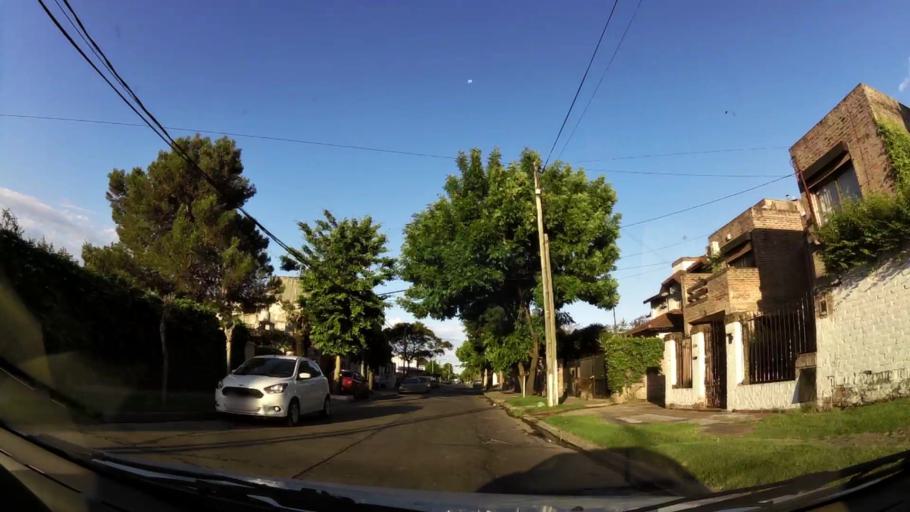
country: AR
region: Buenos Aires
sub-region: Partido de San Isidro
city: San Isidro
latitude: -34.4701
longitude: -58.5514
